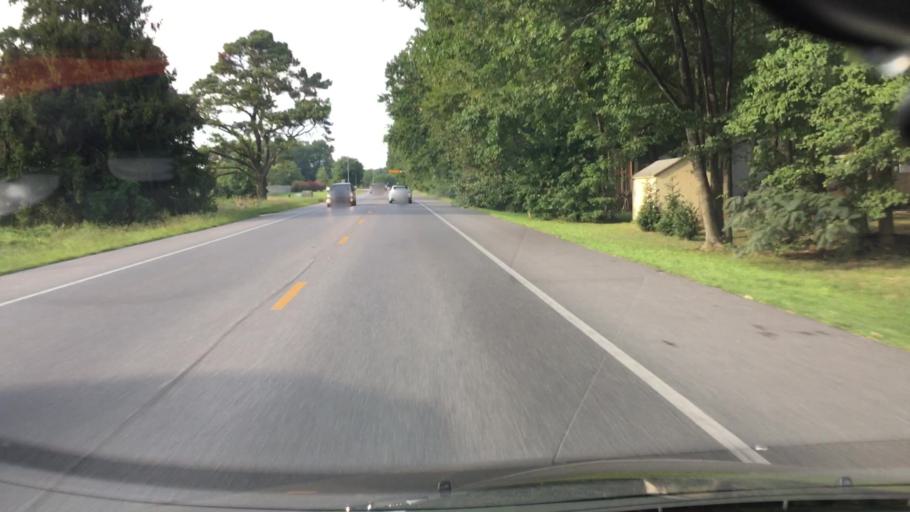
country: US
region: Maryland
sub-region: Worcester County
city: Ocean Pines
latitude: 38.3701
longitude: -75.1642
